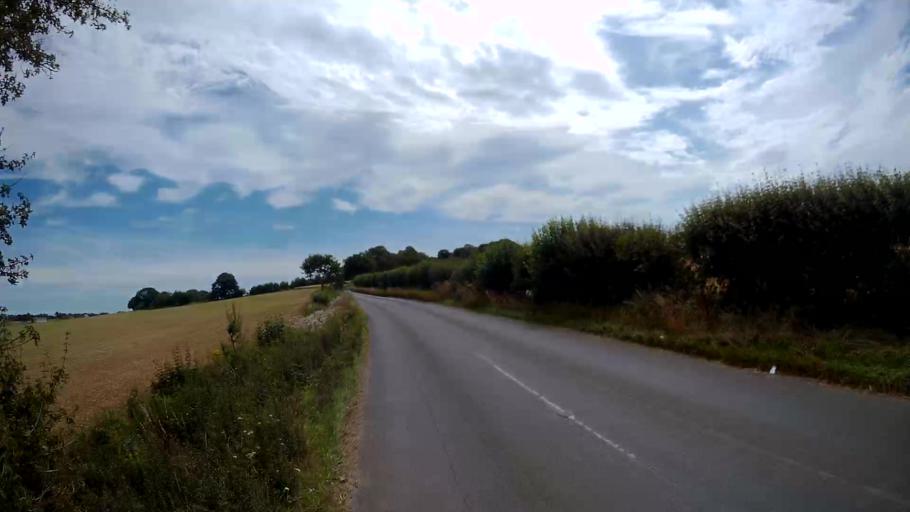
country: GB
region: England
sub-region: Hampshire
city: Long Sutton
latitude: 51.2293
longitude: -0.9587
